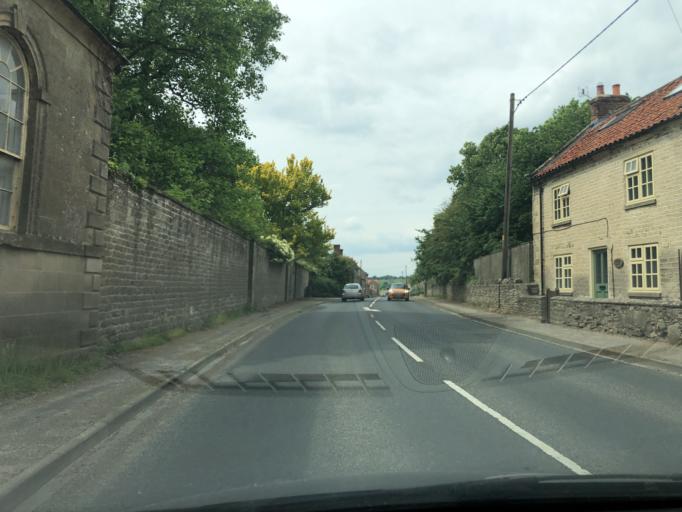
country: GB
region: England
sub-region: North Yorkshire
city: Pickering
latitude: 54.2608
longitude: -0.8088
